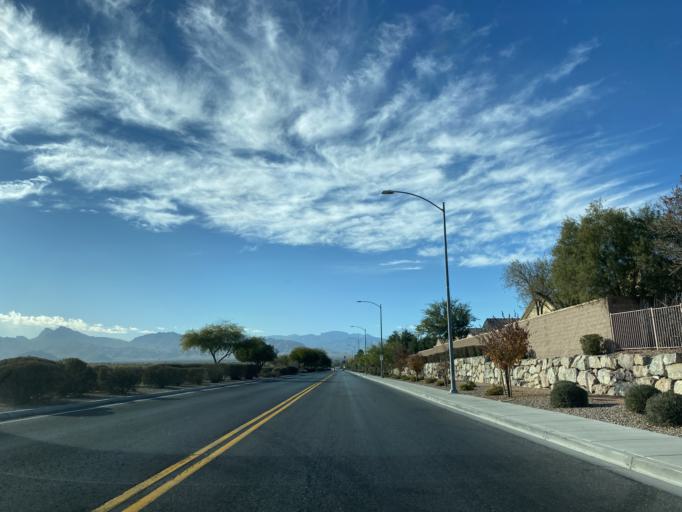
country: US
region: Nevada
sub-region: Clark County
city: North Las Vegas
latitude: 36.3053
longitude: -115.2447
